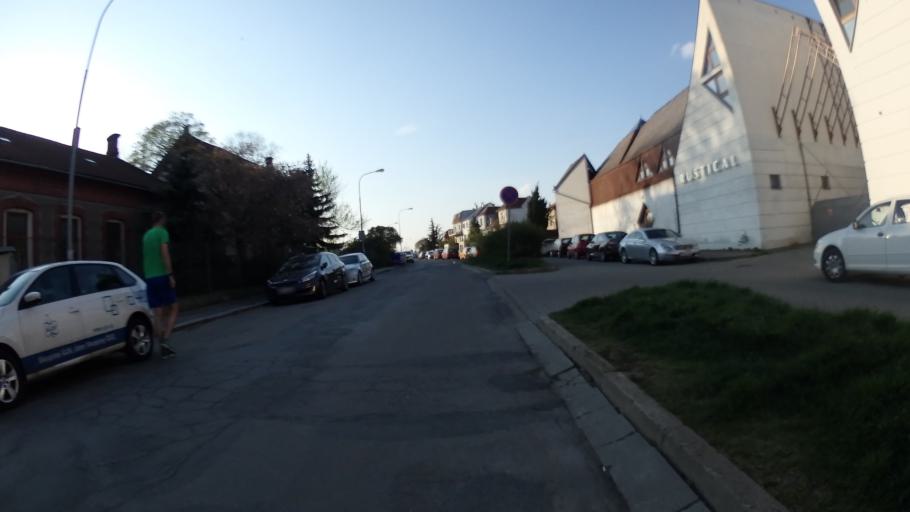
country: CZ
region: South Moravian
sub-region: Mesto Brno
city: Brno
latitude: 49.1818
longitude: 16.5884
